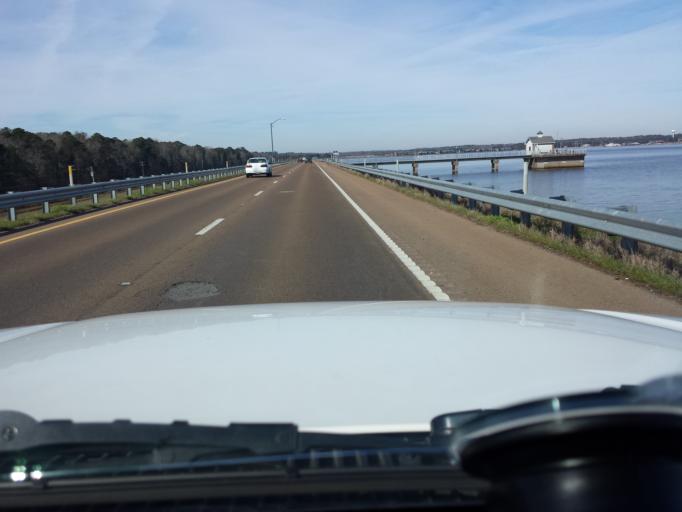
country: US
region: Mississippi
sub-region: Madison County
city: Ridgeland
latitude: 32.4029
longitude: -90.0731
